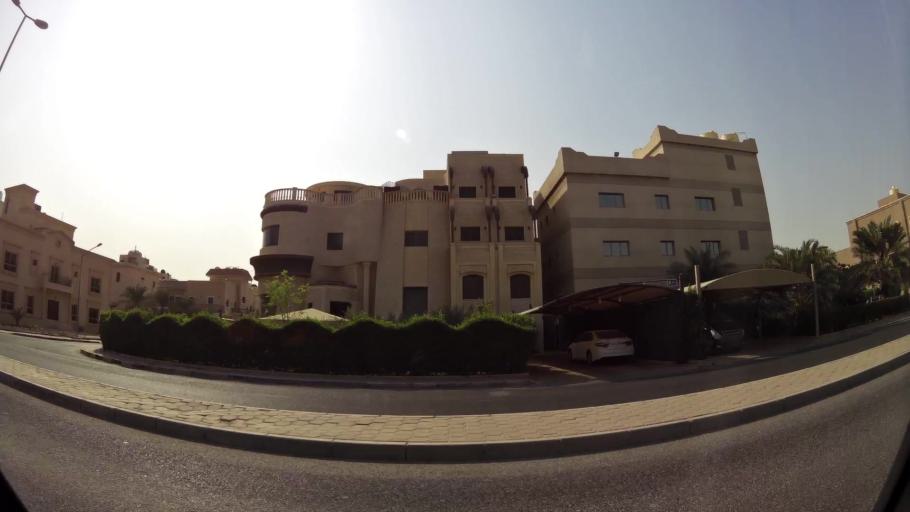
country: KW
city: Bayan
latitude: 29.2869
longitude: 48.0479
